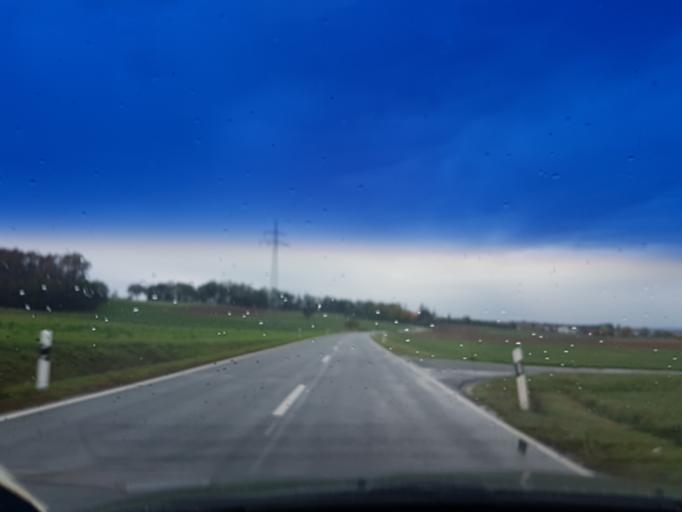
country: DE
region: Bavaria
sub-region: Upper Franconia
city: Pommersfelden
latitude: 49.7655
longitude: 10.7978
